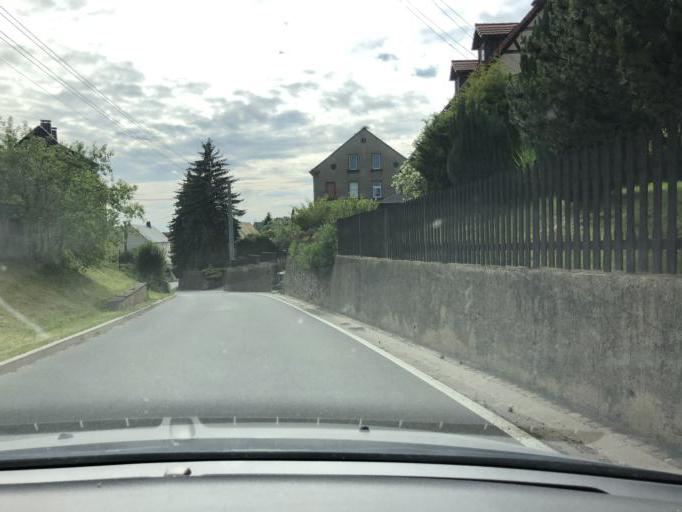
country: DE
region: Saxony
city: Ostrau
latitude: 51.2046
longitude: 12.8331
